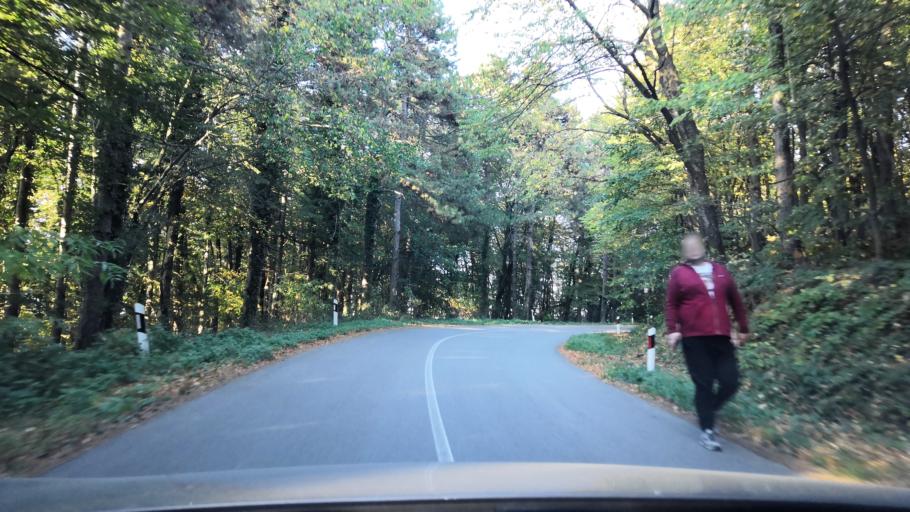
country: RS
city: Vrdnik
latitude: 45.1515
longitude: 19.8324
